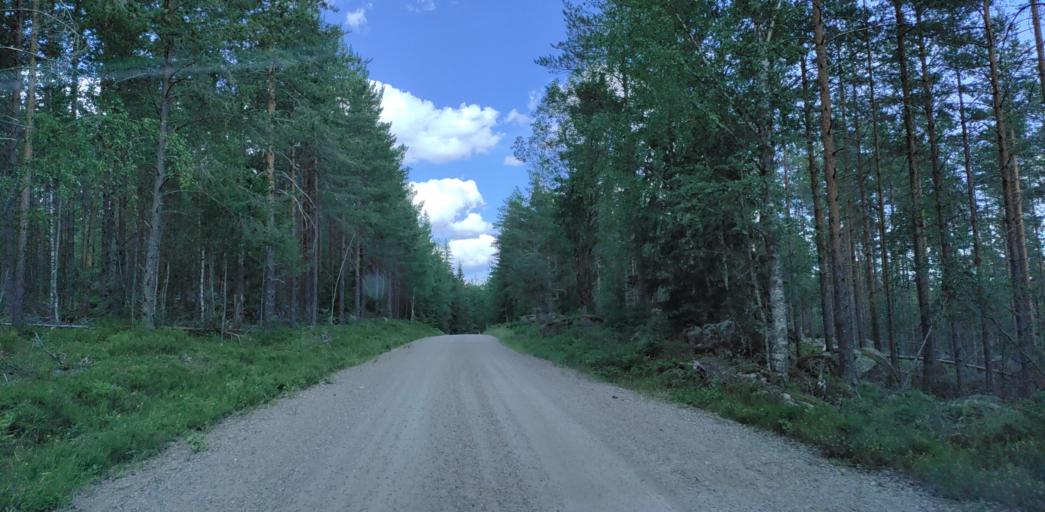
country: SE
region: Vaermland
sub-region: Hagfors Kommun
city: Ekshaerad
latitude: 60.0936
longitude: 13.4170
